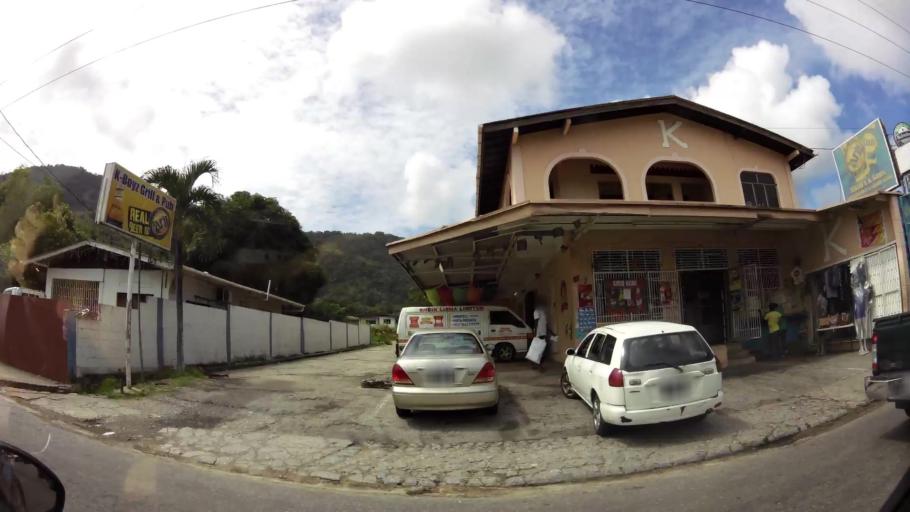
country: TT
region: Diego Martin
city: Petit Valley
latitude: 10.7145
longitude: -61.5616
